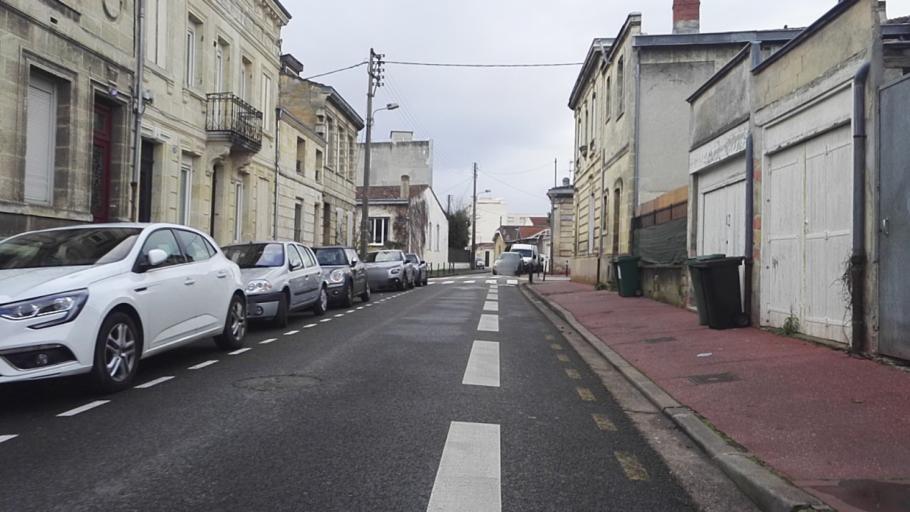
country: FR
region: Aquitaine
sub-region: Departement de la Gironde
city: Le Bouscat
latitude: 44.8461
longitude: -0.6025
